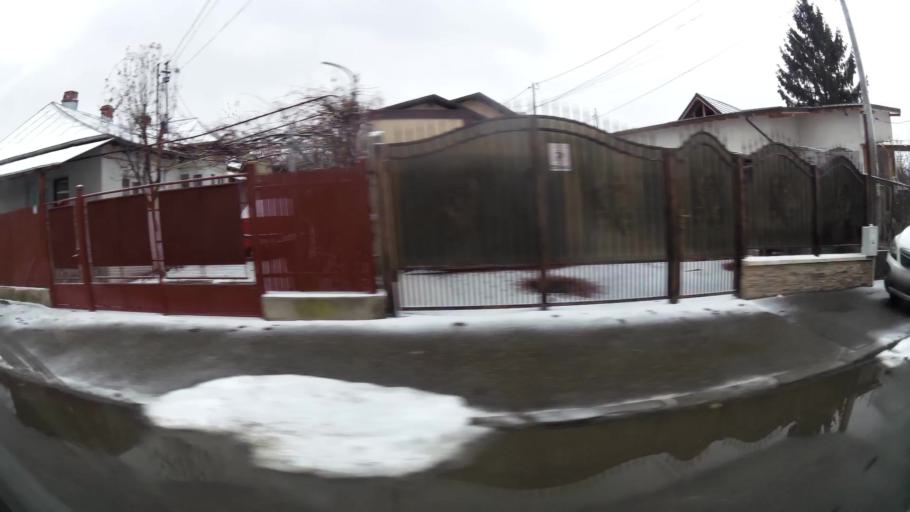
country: RO
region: Prahova
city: Ploiesti
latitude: 44.9326
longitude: 26.0481
